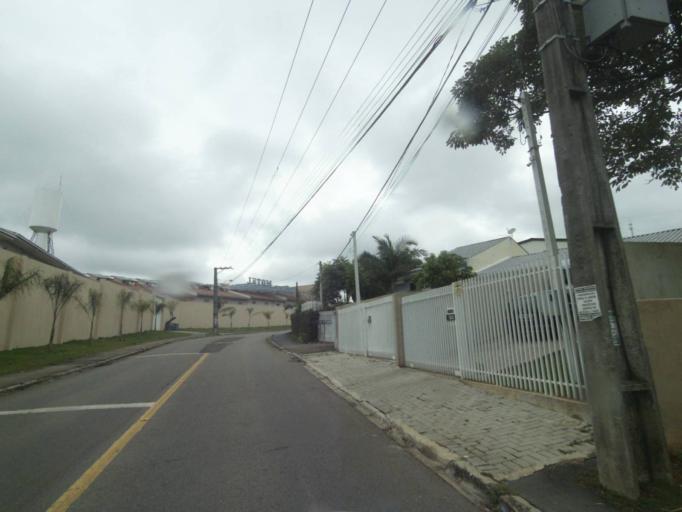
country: BR
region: Parana
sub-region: Curitiba
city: Curitiba
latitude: -25.4294
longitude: -49.3374
